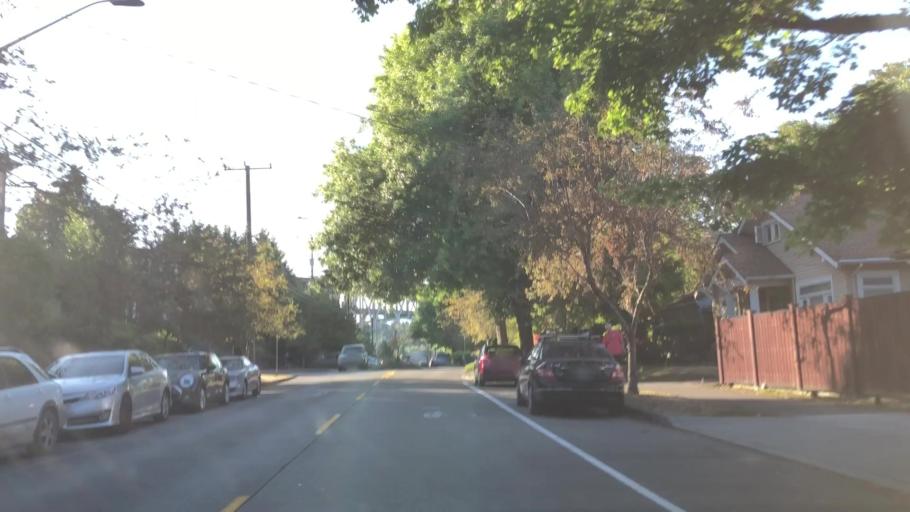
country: US
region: Washington
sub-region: King County
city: Seattle
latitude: 47.6494
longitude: -122.3193
